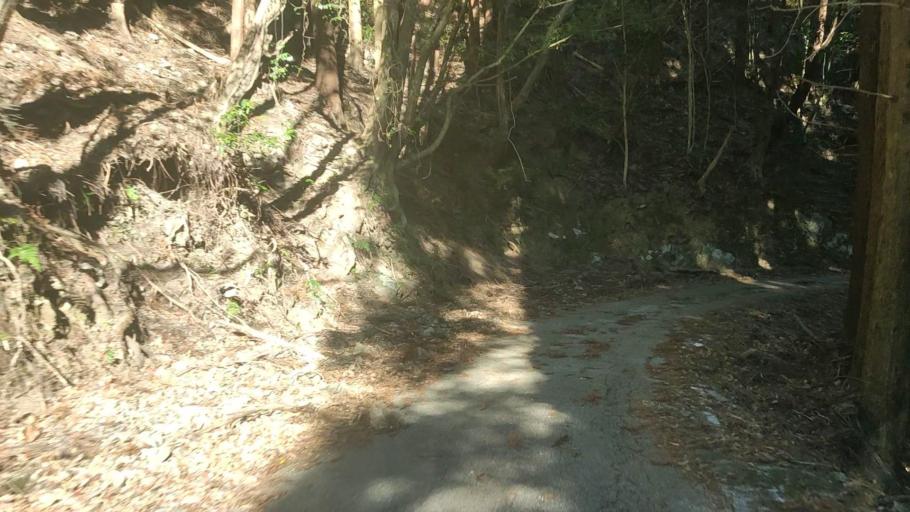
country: JP
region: Oita
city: Saiki
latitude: 32.7848
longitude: 131.8516
